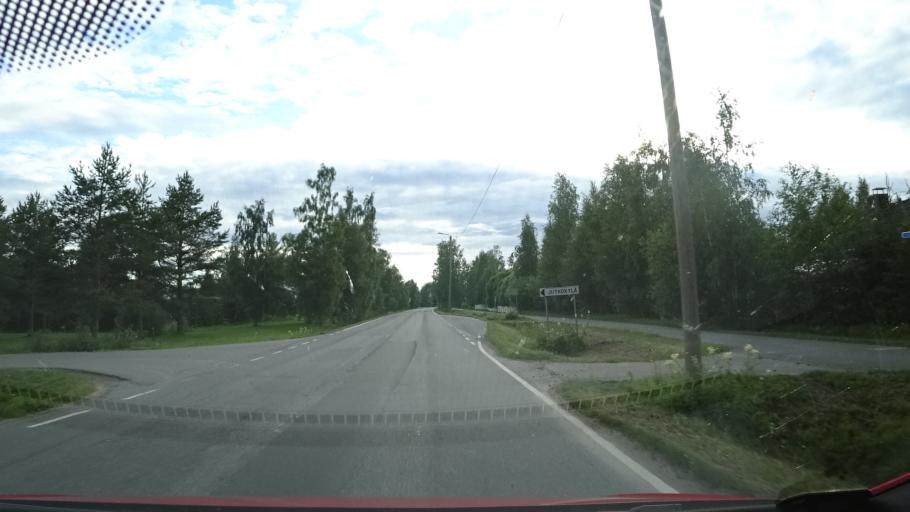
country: FI
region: Northern Ostrobothnia
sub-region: Oulu
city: Liminka
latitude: 64.8082
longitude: 25.4465
